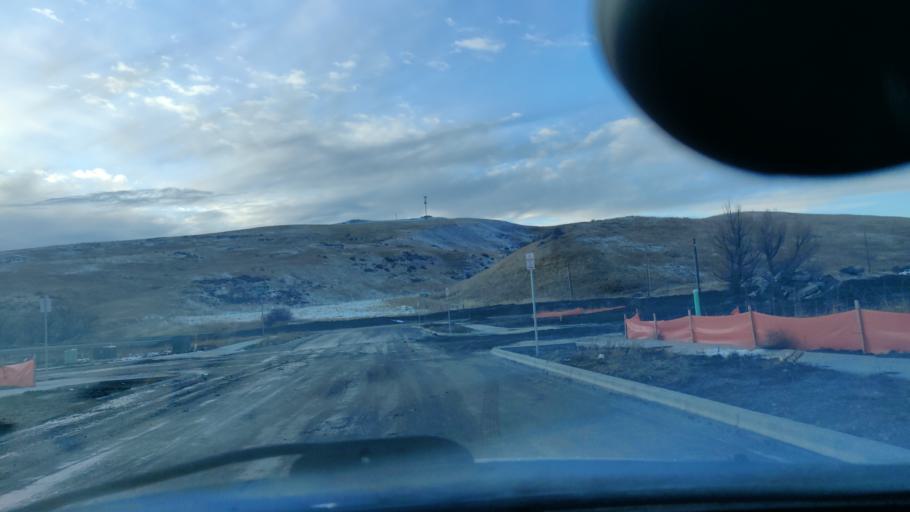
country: US
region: Idaho
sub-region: Ada County
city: Eagle
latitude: 43.7920
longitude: -116.2616
